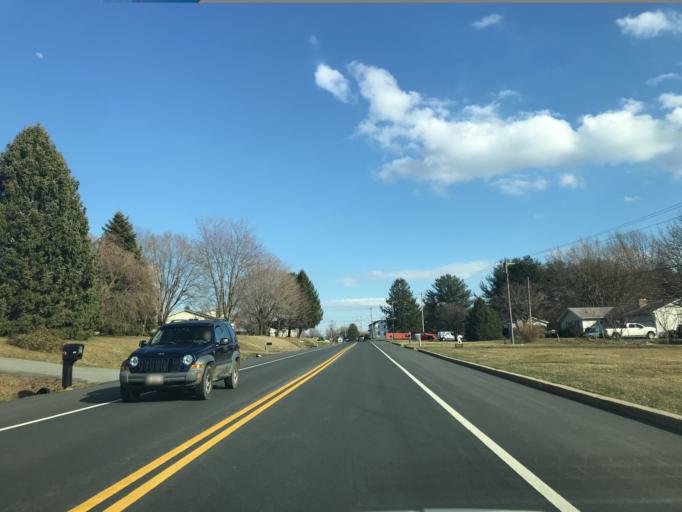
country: US
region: Maryland
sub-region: Cecil County
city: Rising Sun
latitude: 39.6919
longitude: -76.0512
